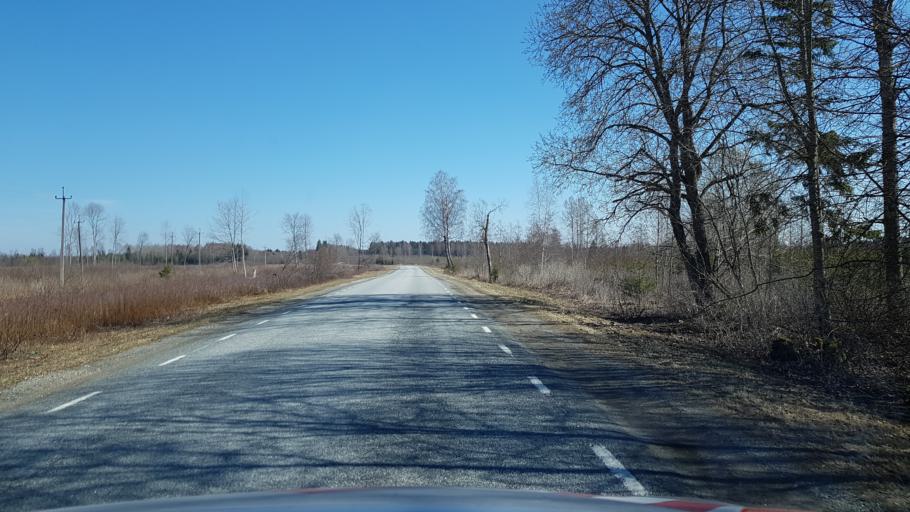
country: EE
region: Laeaene-Virumaa
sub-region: Vaeike-Maarja vald
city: Vaike-Maarja
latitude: 59.1255
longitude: 26.2801
